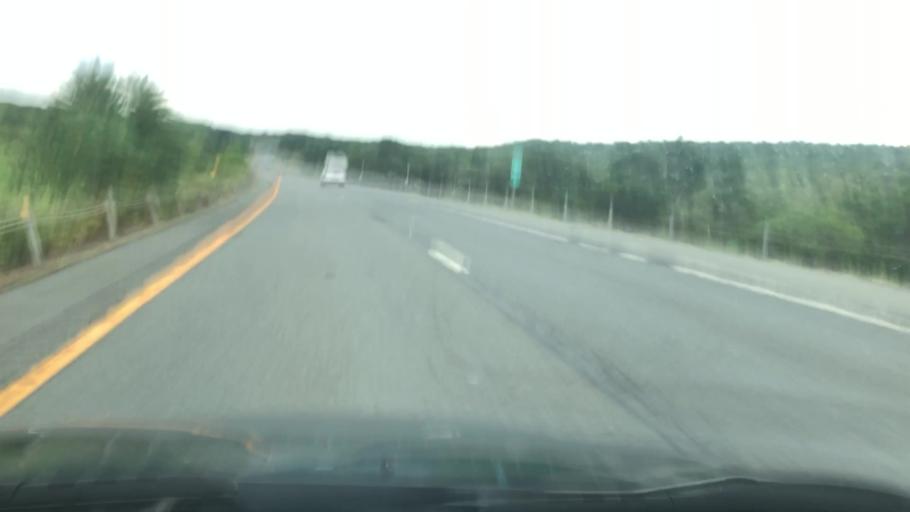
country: US
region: New York
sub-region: Orange County
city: Otisville
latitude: 41.3842
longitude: -74.5755
